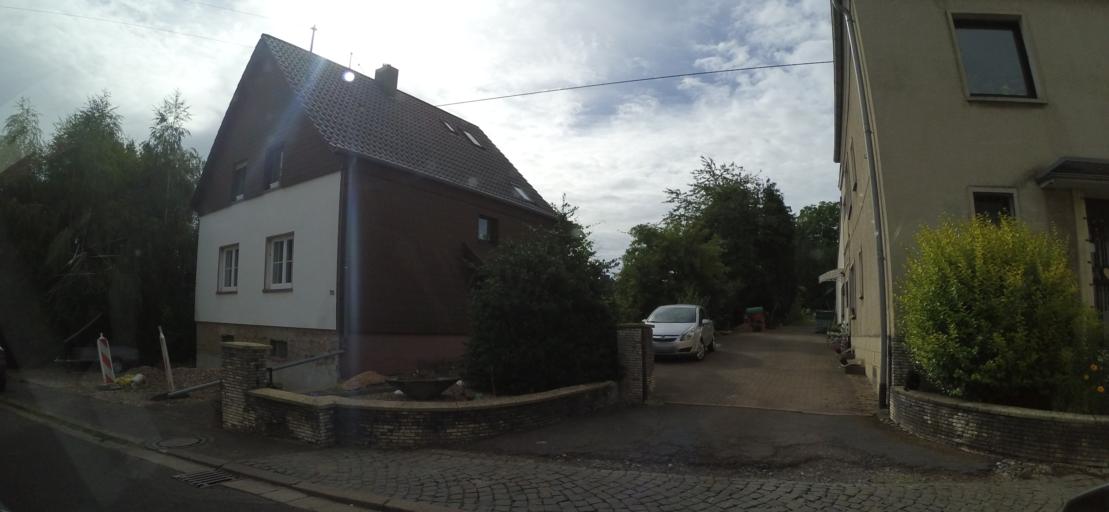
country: DE
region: Saarland
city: Riegelsberg
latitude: 49.3217
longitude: 6.9086
